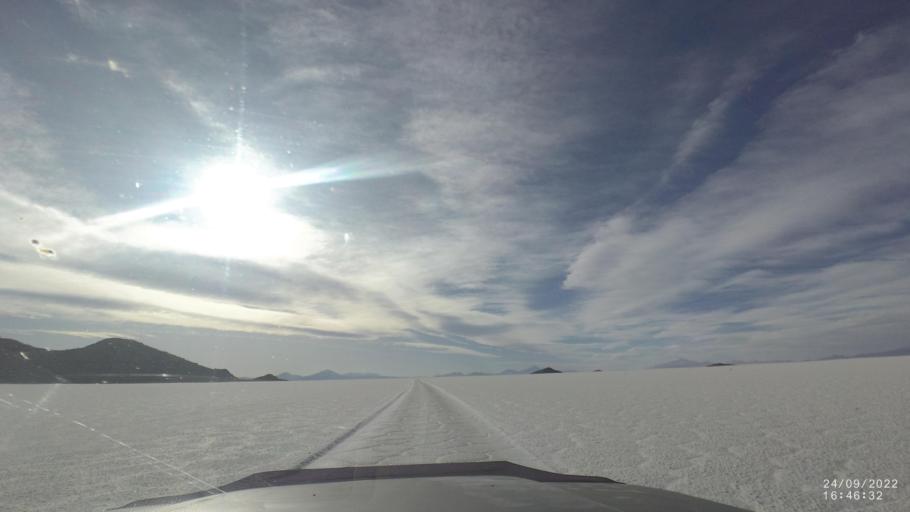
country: BO
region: Potosi
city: Colchani
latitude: -20.1371
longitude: -67.7915
